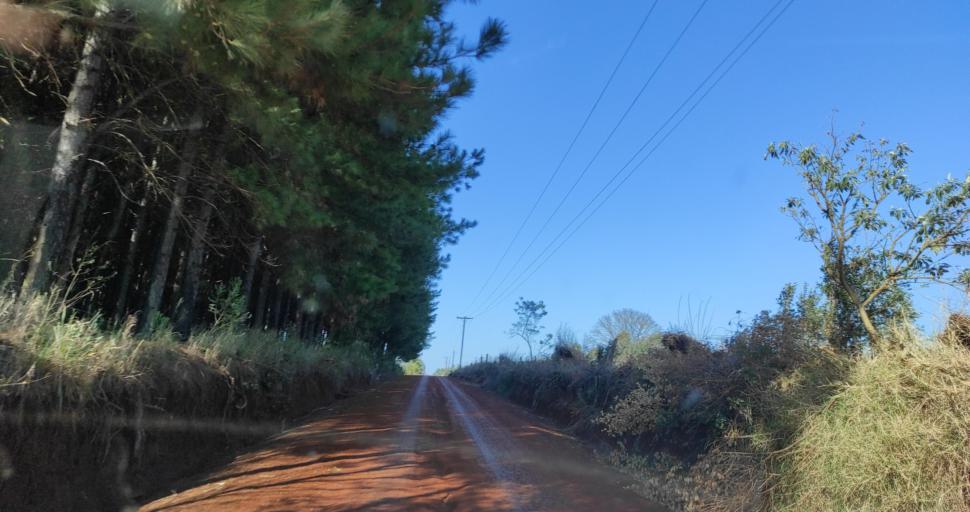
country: AR
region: Misiones
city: Capiovi
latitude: -26.9014
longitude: -55.0501
